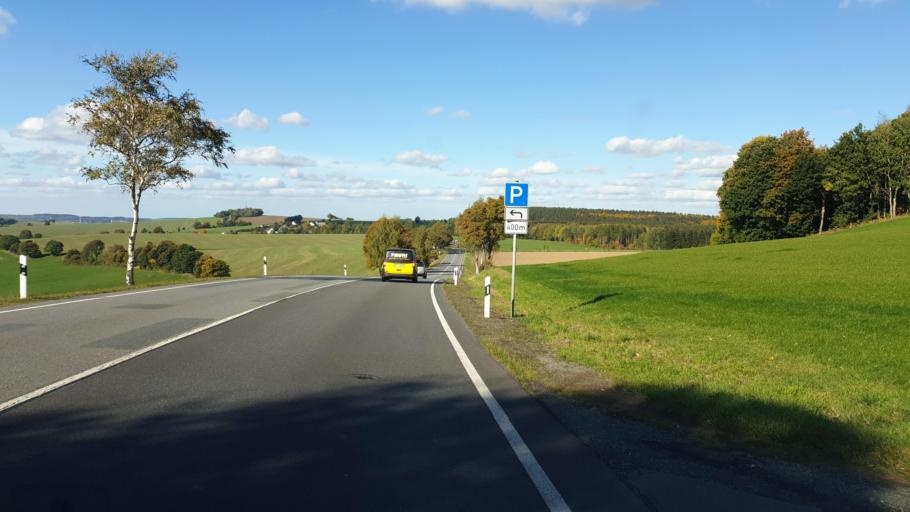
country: DE
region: Saxony
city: Grossolbersdorf
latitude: 50.6944
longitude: 13.1121
